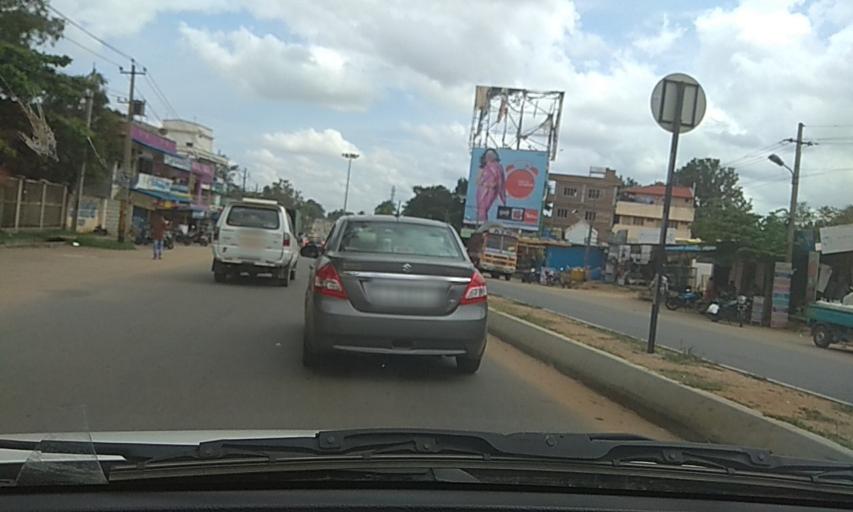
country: IN
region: Karnataka
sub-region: Tumkur
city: Tumkur
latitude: 13.3759
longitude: 77.0994
